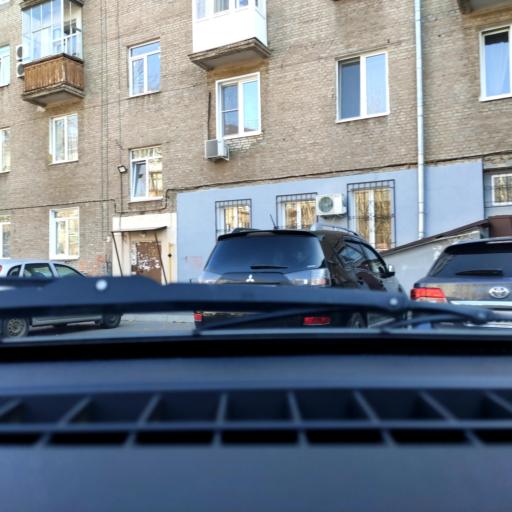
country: RU
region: Bashkortostan
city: Ufa
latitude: 54.8196
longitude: 56.0629
